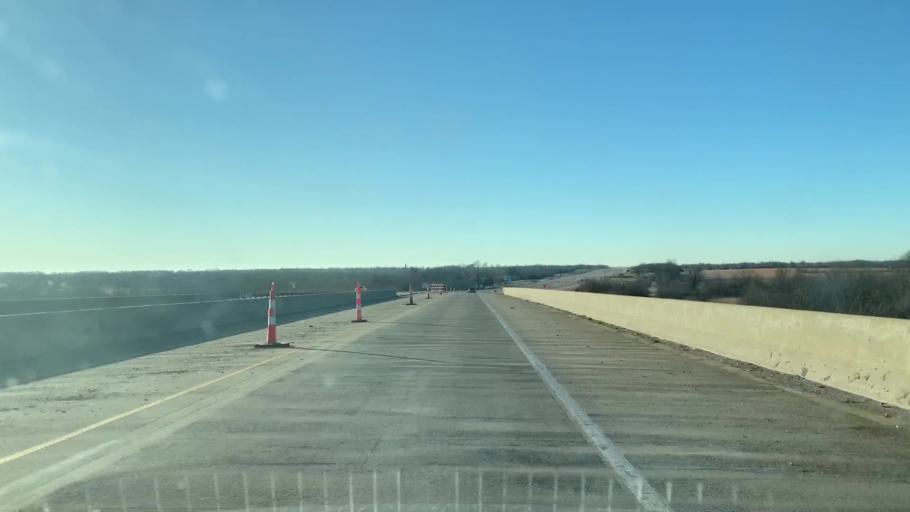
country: US
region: Kansas
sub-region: Bourbon County
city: Fort Scott
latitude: 37.7677
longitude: -94.7055
